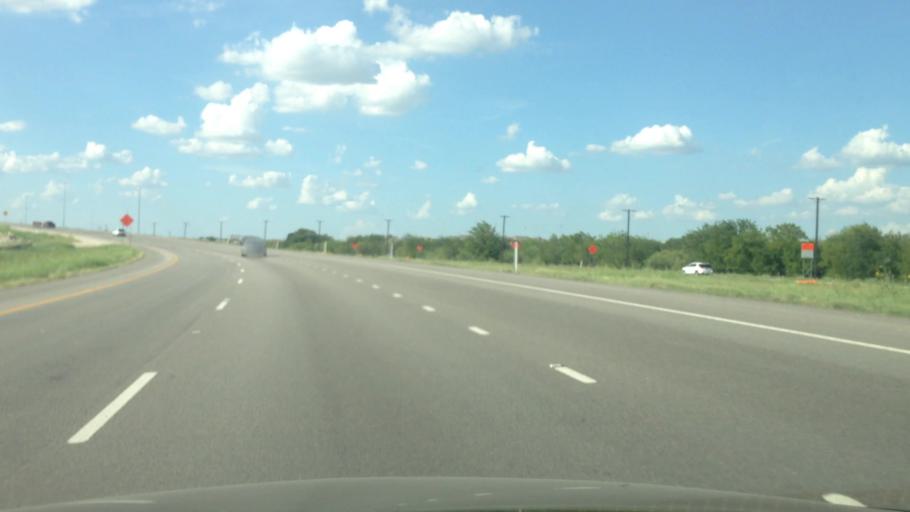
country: US
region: Texas
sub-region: Tarrant County
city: Blue Mound
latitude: 32.8831
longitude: -97.3153
